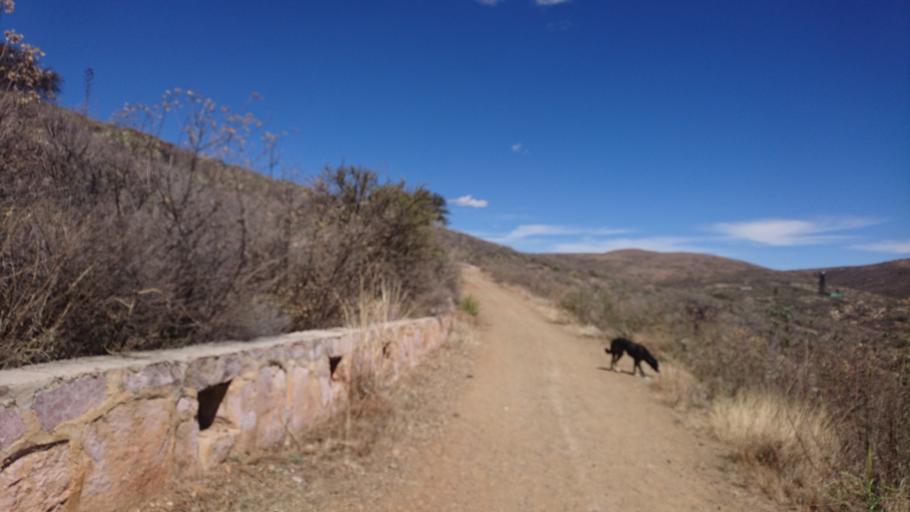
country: MX
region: Zacatecas
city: Zacatecas
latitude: 22.7800
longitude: -102.5468
